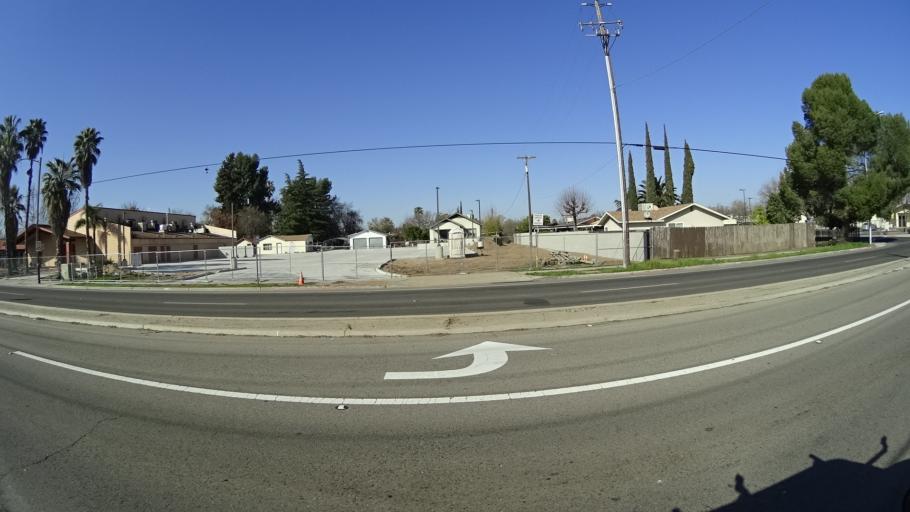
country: US
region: California
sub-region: Fresno County
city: Fresno
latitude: 36.7119
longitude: -119.7364
